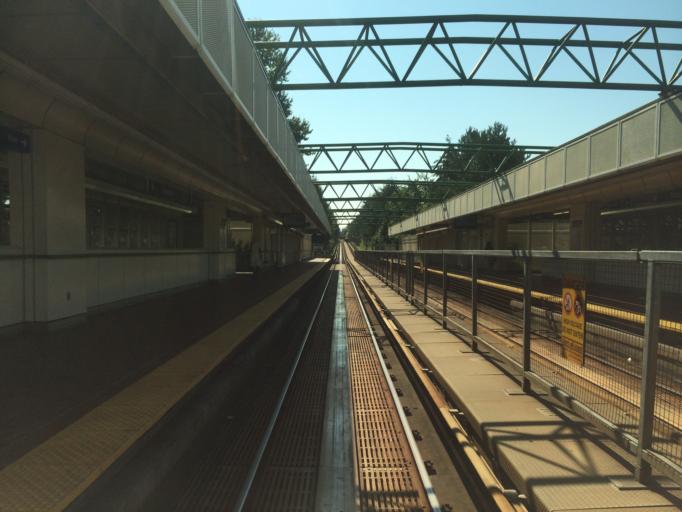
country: CA
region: British Columbia
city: Vancouver
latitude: 49.2484
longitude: -123.0559
